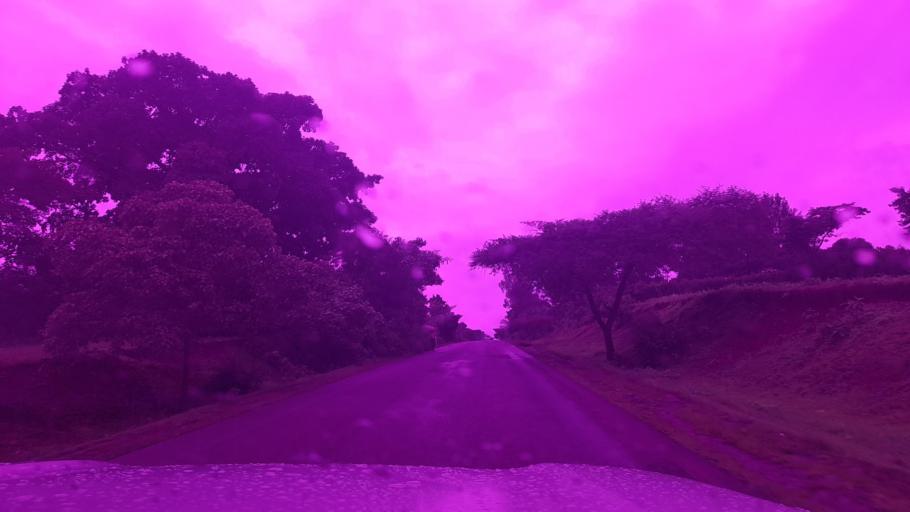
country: ET
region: Oromiya
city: Jima
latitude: 7.7199
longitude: 37.2561
